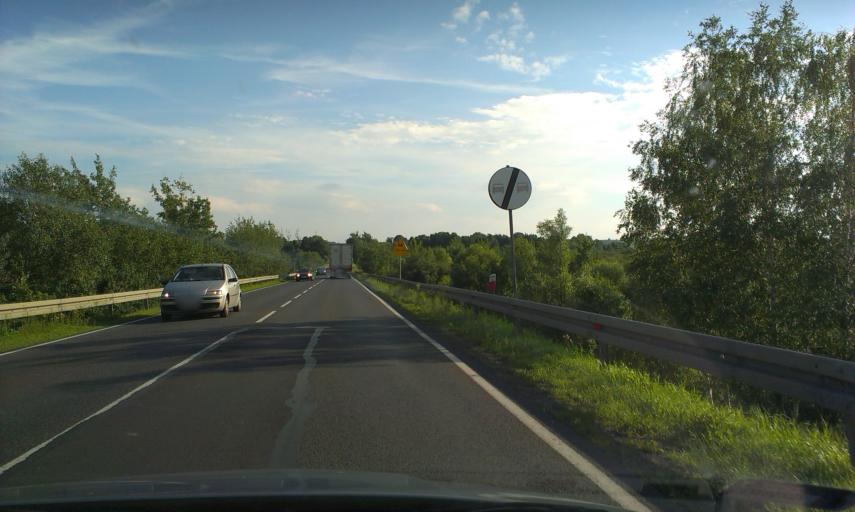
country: PL
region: Kujawsko-Pomorskie
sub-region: Powiat bydgoski
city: Biale Blota
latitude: 53.1512
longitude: 17.8854
